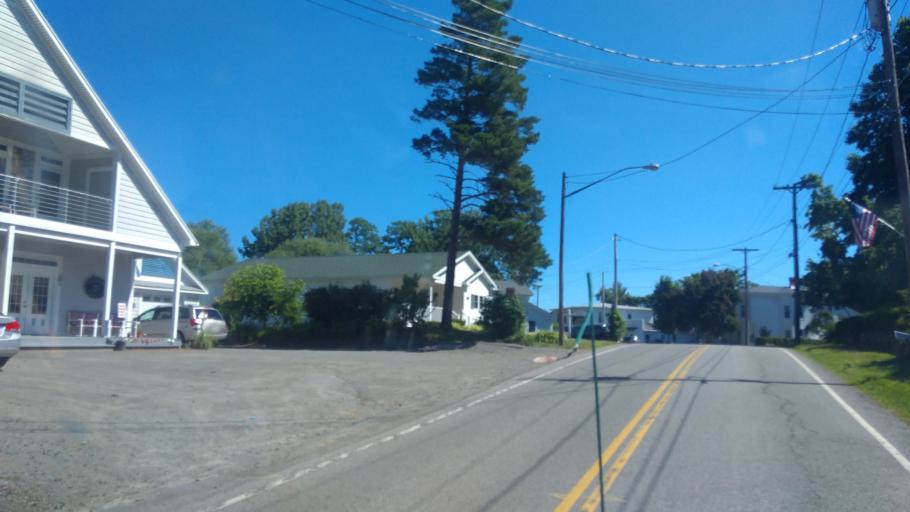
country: US
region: New York
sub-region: Wayne County
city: Williamson
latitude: 43.2808
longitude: -77.1843
